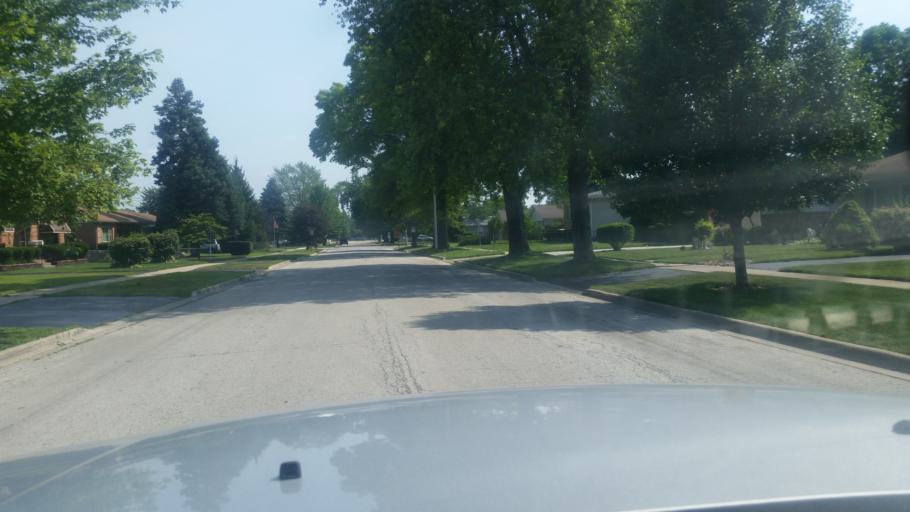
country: US
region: Illinois
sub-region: Cook County
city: Chicago Ridge
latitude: 41.6933
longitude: -87.7765
